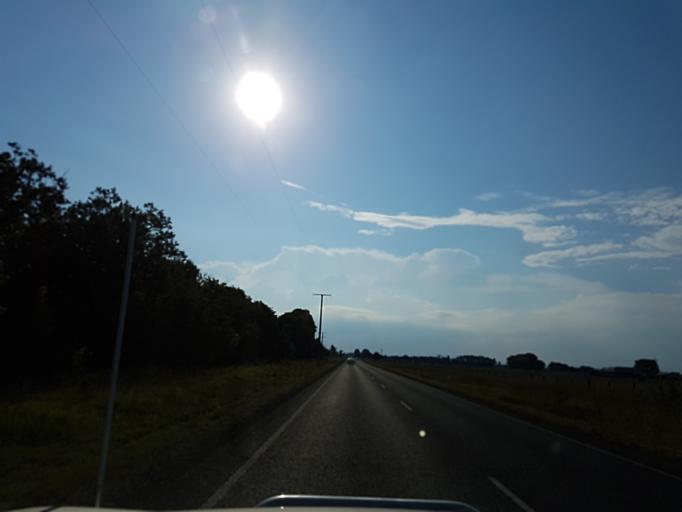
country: AU
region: Victoria
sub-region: Wellington
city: Sale
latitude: -38.0661
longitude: 147.0588
